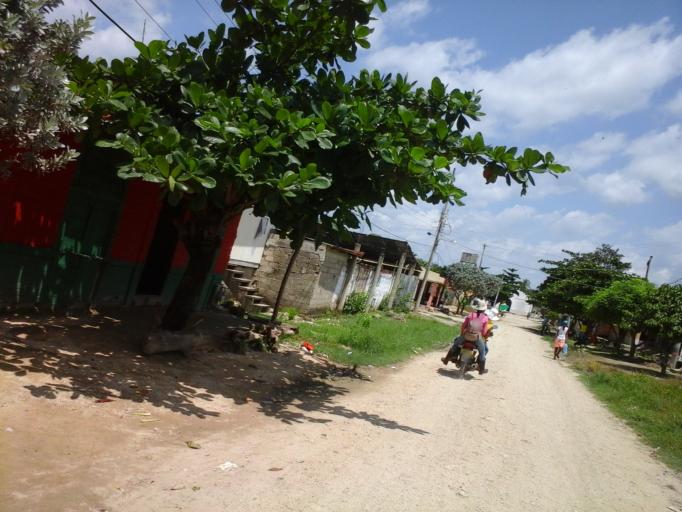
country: CO
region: Bolivar
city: San Pablo
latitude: 10.1464
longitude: -75.2772
